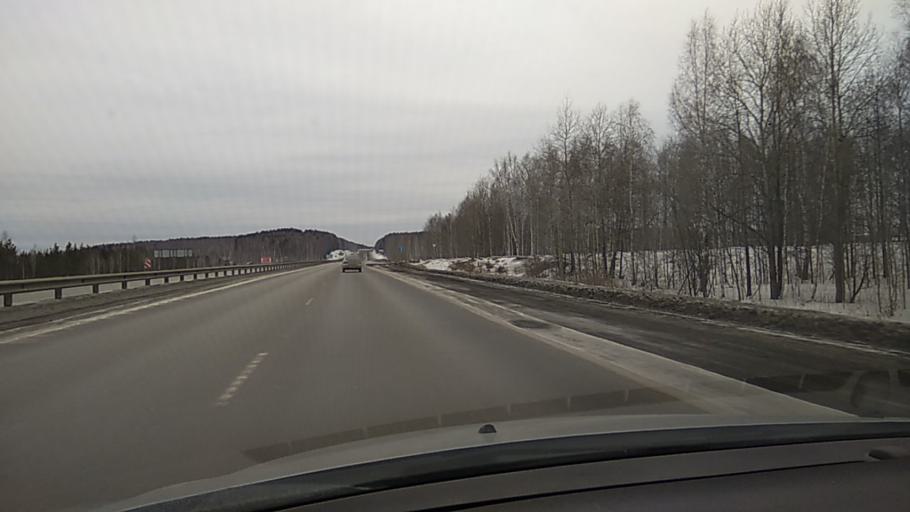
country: RU
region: Sverdlovsk
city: Talitsa
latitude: 56.8378
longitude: 60.1469
